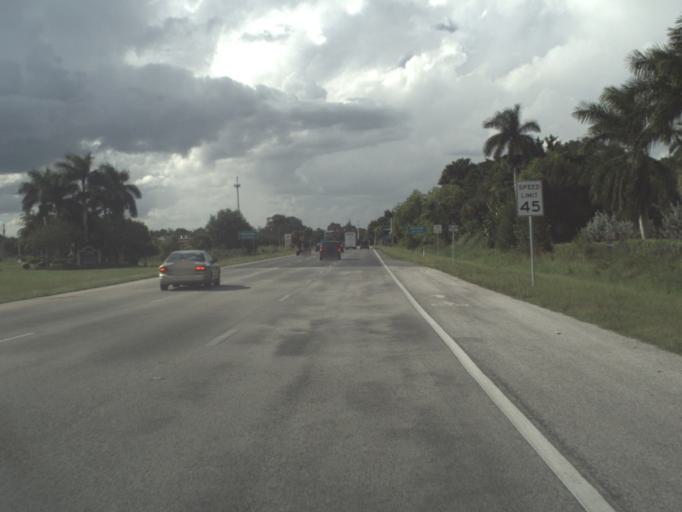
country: US
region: Florida
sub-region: Charlotte County
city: Punta Gorda
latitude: 26.9405
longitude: -82.0293
